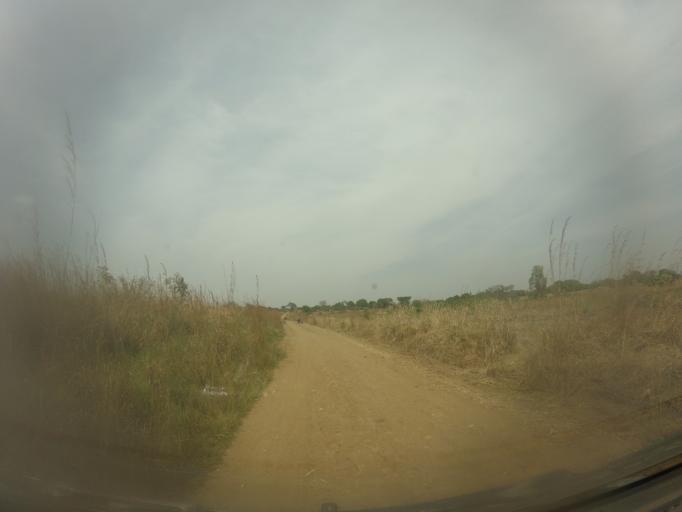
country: UG
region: Northern Region
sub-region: Arua District
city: Arua
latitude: 2.7688
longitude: 31.0357
